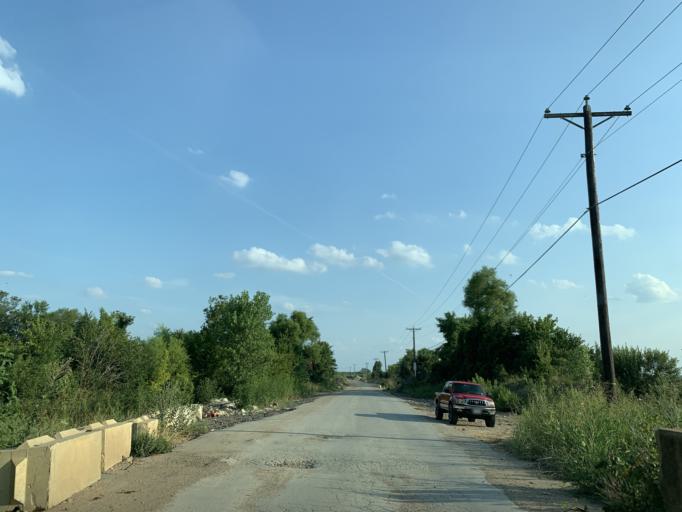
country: US
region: Texas
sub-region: Tarrant County
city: Hurst
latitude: 32.7982
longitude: -97.1692
